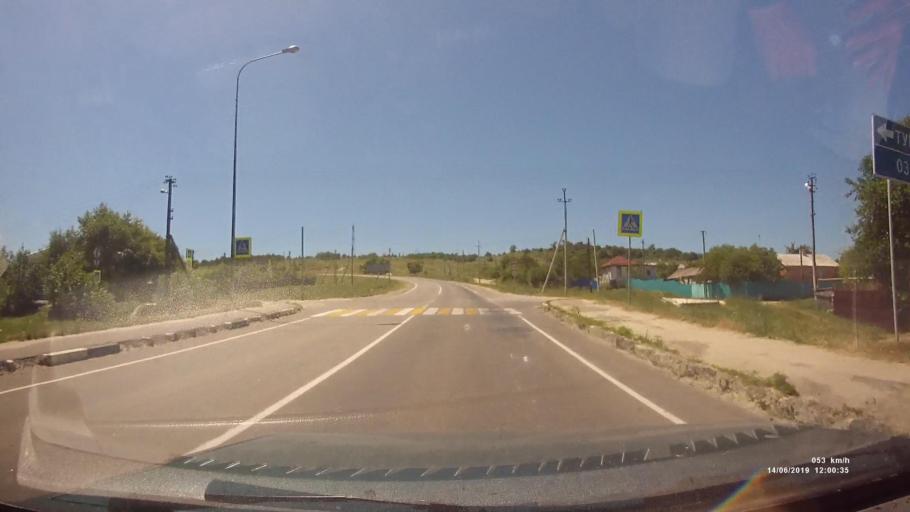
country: RU
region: Rostov
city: Kazanskaya
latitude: 49.7880
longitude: 41.1259
